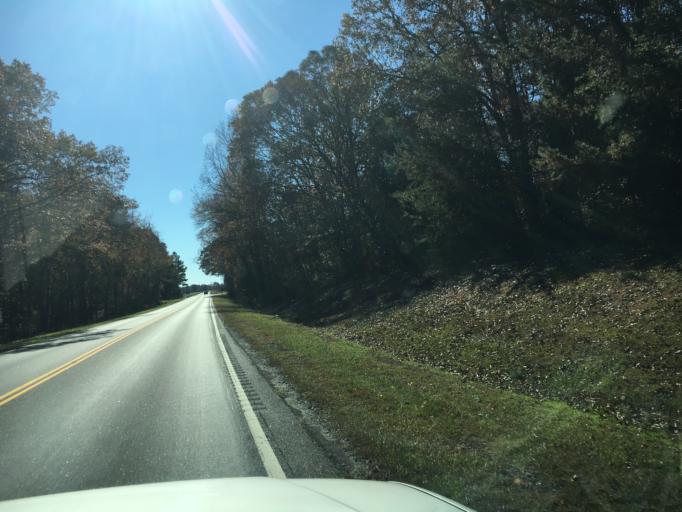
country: US
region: Georgia
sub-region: Hart County
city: Hartwell
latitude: 34.3781
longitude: -82.8117
